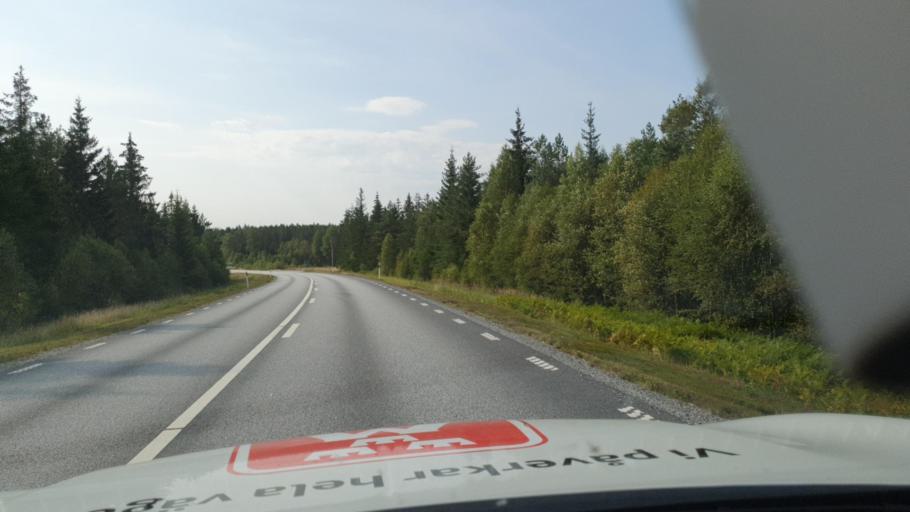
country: SE
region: Vaestra Goetaland
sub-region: Tanums Kommun
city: Tanumshede
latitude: 58.8324
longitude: 11.6115
